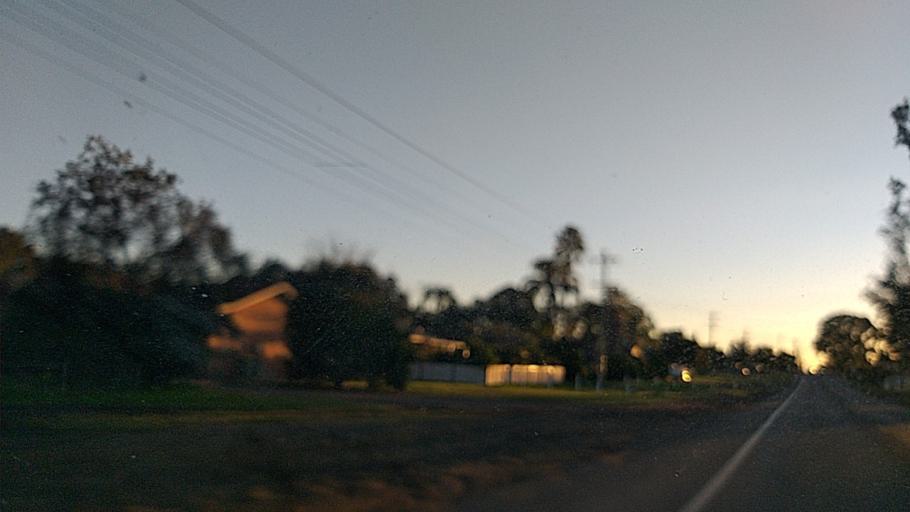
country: AU
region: New South Wales
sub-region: Hawkesbury
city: South Windsor
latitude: -33.6276
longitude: 150.7960
